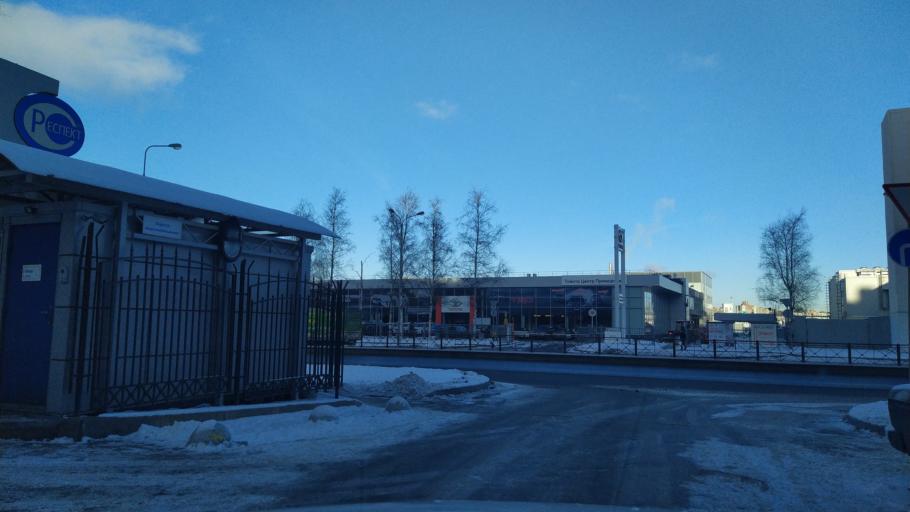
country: RU
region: St.-Petersburg
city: Staraya Derevnya
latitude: 59.9887
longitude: 30.2222
